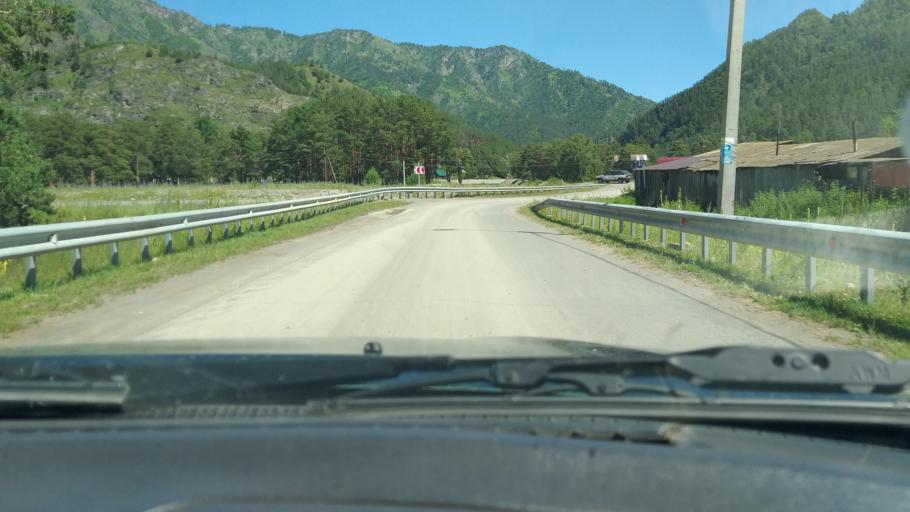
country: RU
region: Altay
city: Chemal
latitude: 51.3909
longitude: 86.0208
